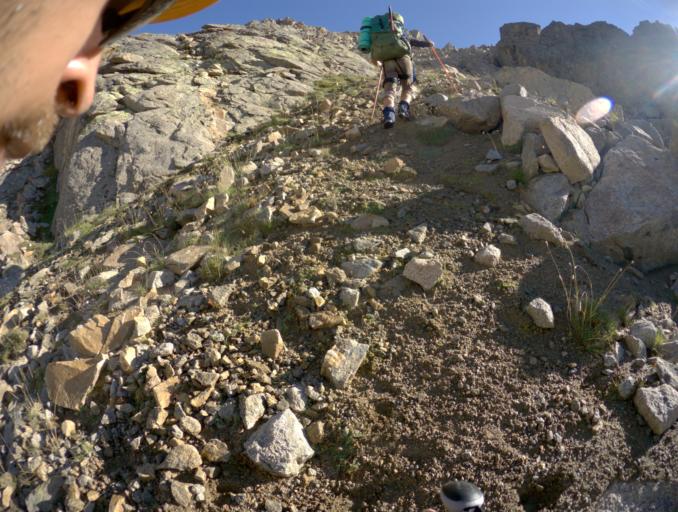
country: RU
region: Kabardino-Balkariya
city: Terskol
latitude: 43.3277
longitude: 42.5339
